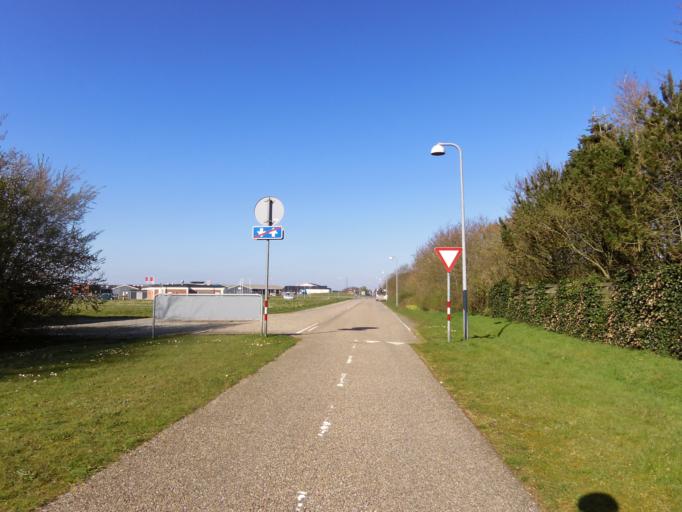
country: DK
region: South Denmark
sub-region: Esbjerg Kommune
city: Ribe
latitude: 55.3501
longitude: 8.7810
